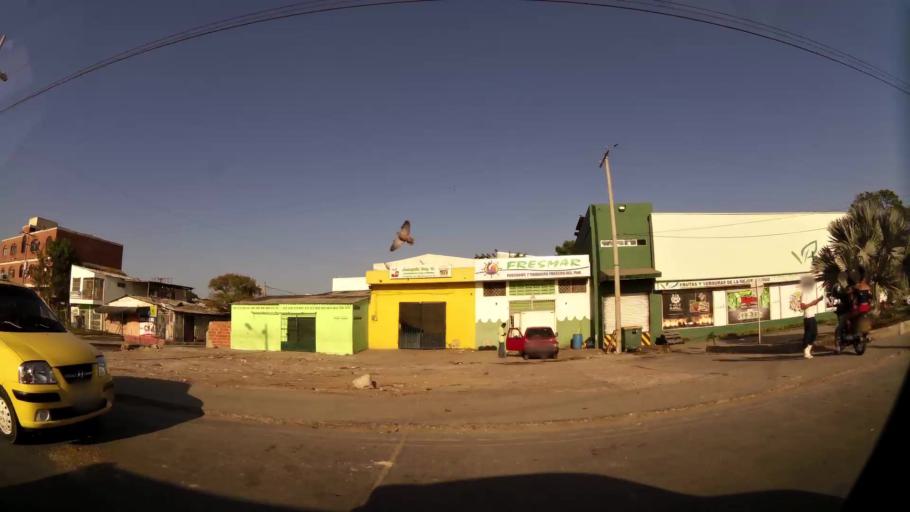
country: CO
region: Bolivar
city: Cartagena
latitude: 10.4102
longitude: -75.5237
